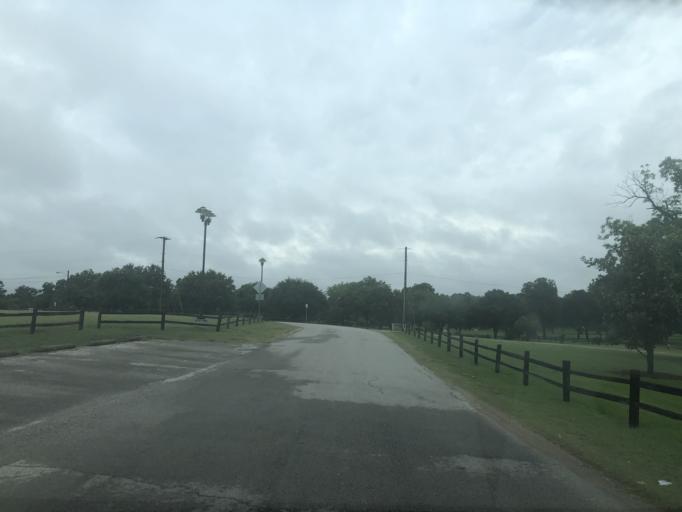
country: US
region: Texas
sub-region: Dallas County
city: Irving
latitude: 32.7965
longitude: -96.9399
